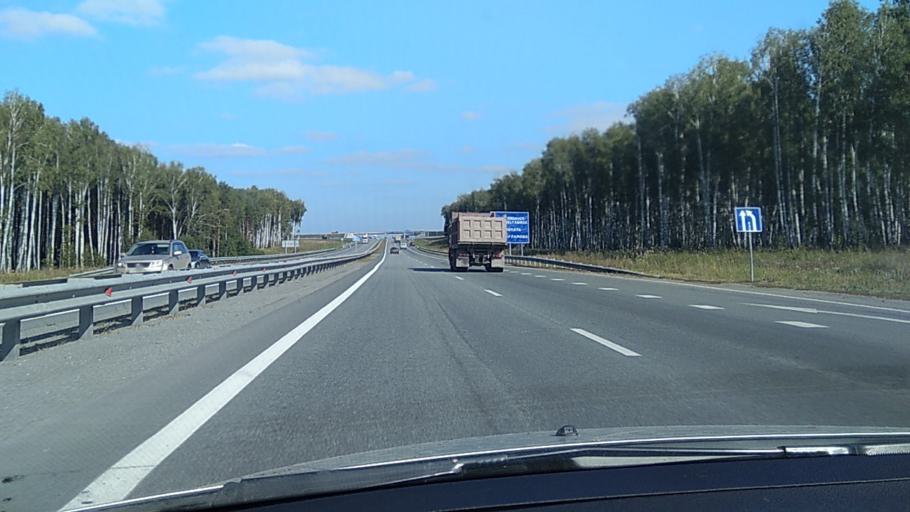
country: RU
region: Chelyabinsk
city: Timiryazevskiy
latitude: 54.9390
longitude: 60.7832
